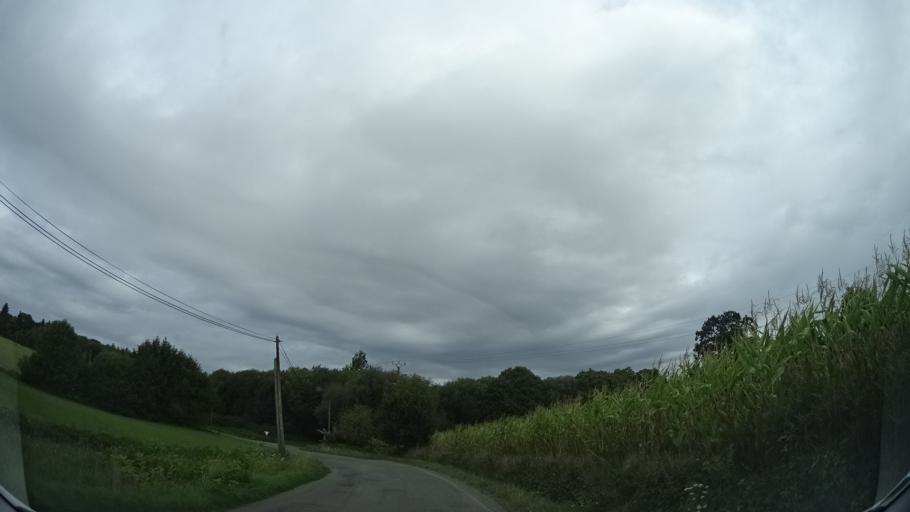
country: FR
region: Brittany
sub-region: Departement d'Ille-et-Vilaine
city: Tinteniac
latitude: 48.2899
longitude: -1.8683
